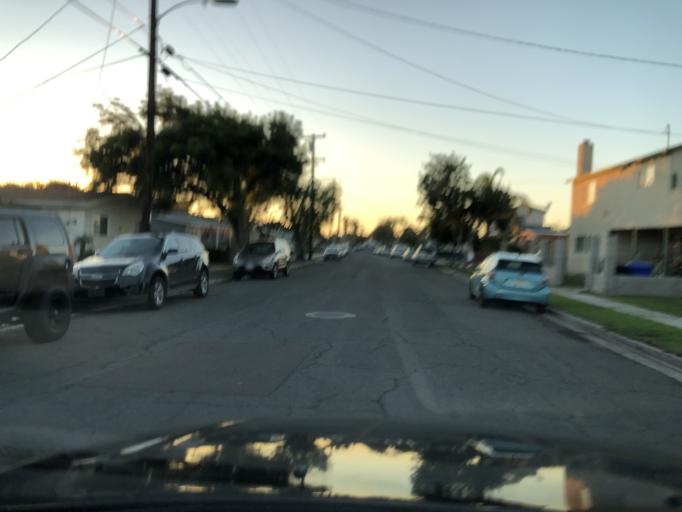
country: US
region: California
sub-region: San Diego County
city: La Jolla
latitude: 32.8353
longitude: -117.1769
